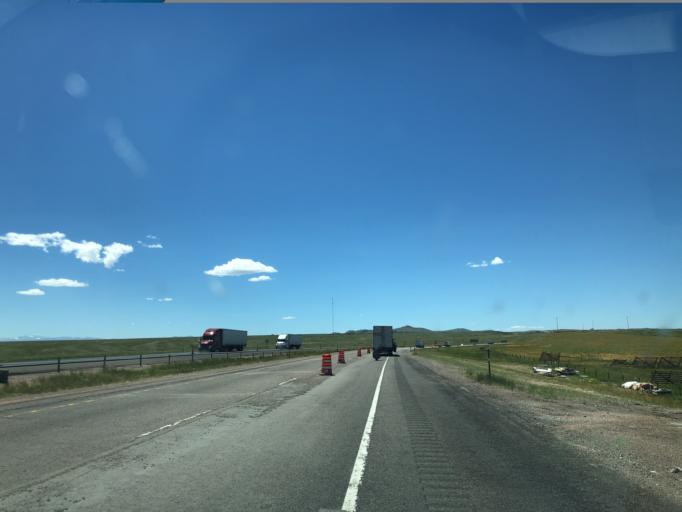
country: US
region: Wyoming
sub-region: Laramie County
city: Cheyenne
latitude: 41.0983
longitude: -105.1002
